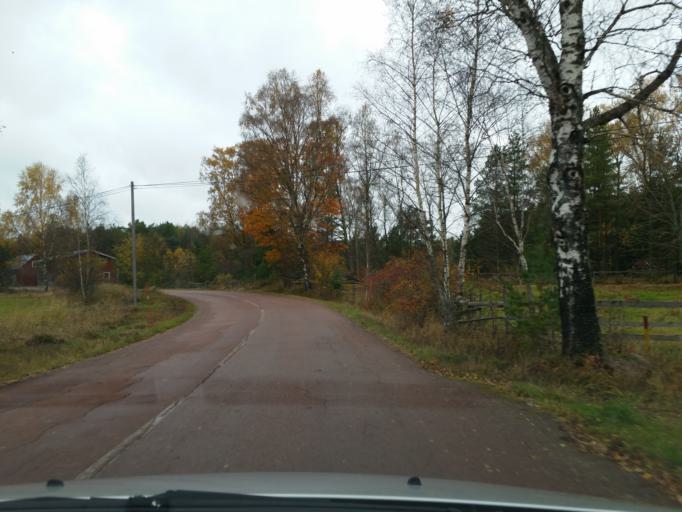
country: AX
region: Alands landsbygd
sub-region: Lumparland
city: Lumparland
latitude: 60.1266
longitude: 20.2409
